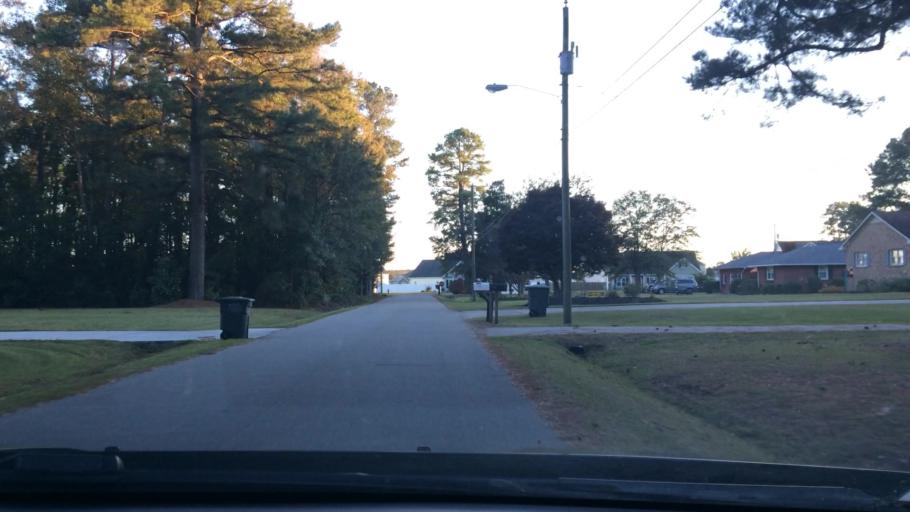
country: US
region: North Carolina
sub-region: Pitt County
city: Ayden
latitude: 35.4708
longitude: -77.4375
